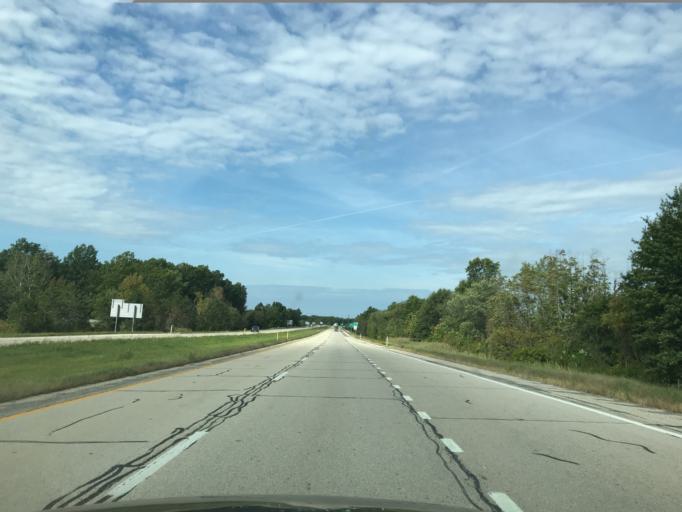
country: US
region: Ohio
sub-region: Ashtabula County
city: Edgewood
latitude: 41.8788
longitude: -80.7661
